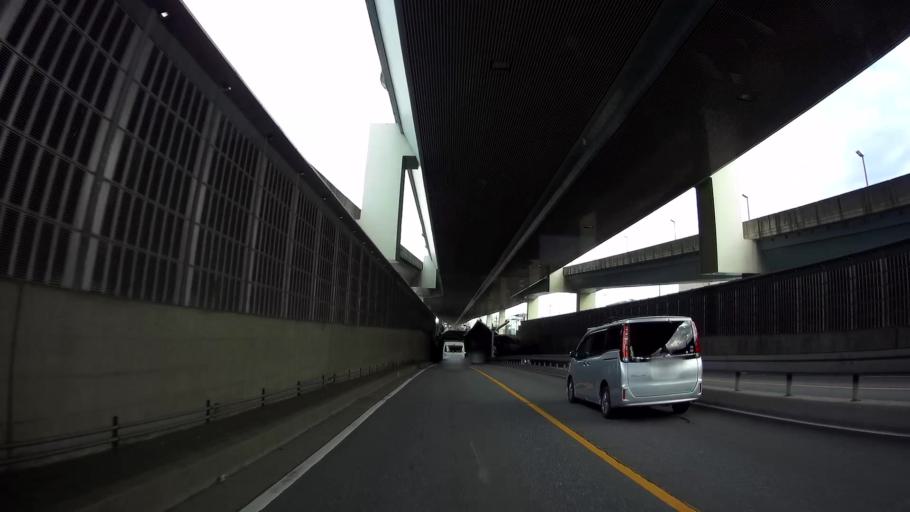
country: JP
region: Saitama
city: Yono
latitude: 35.8677
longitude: 139.6203
